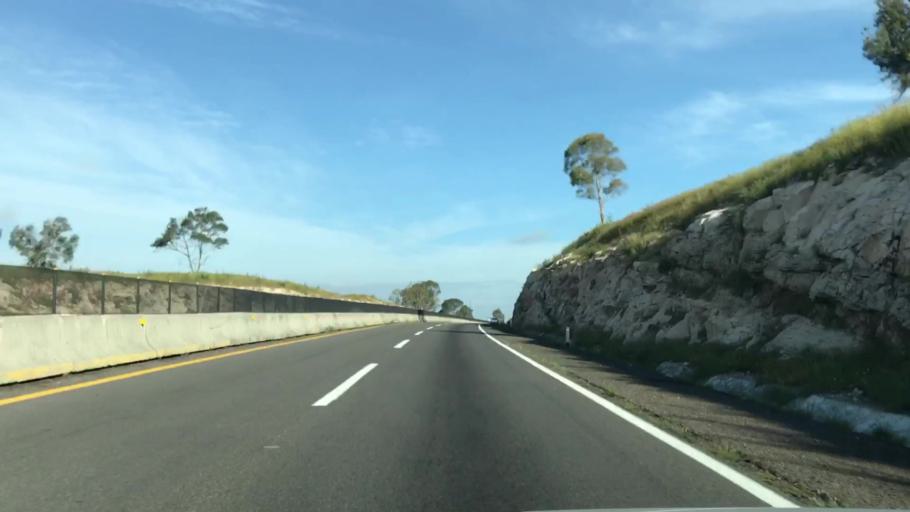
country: MX
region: Jalisco
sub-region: Lagos de Moreno
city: Cristeros [Fraccionamiento]
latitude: 21.3712
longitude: -102.1322
